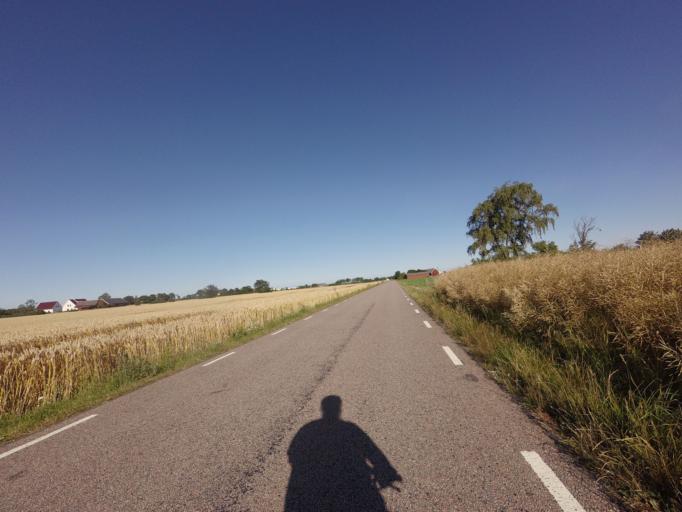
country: SE
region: Skane
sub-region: Hoganas Kommun
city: Hoganas
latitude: 56.1617
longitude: 12.6135
